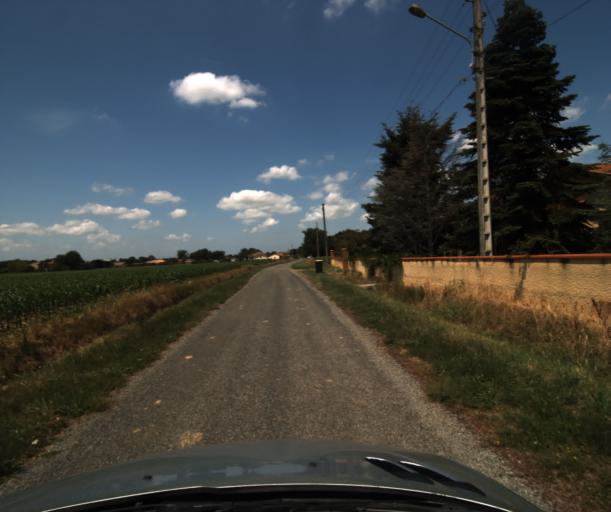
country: FR
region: Midi-Pyrenees
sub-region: Departement de la Haute-Garonne
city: Saint-Lys
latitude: 43.4731
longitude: 1.1945
